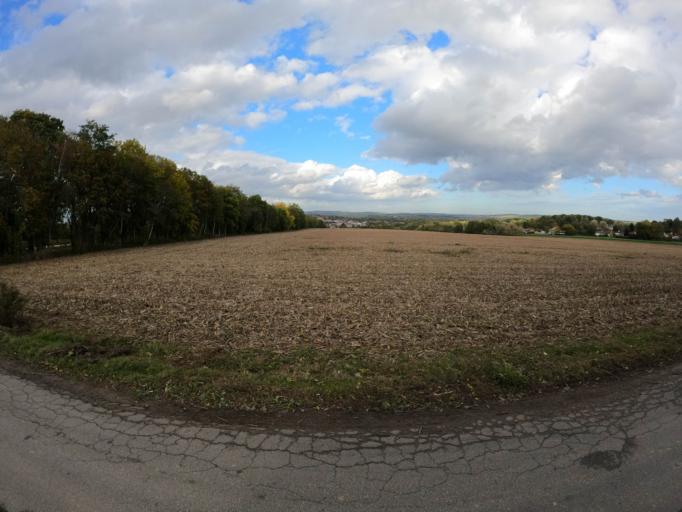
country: FR
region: Ile-de-France
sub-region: Departement de Seine-et-Marne
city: Coupvray
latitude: 48.8885
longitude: 2.8036
